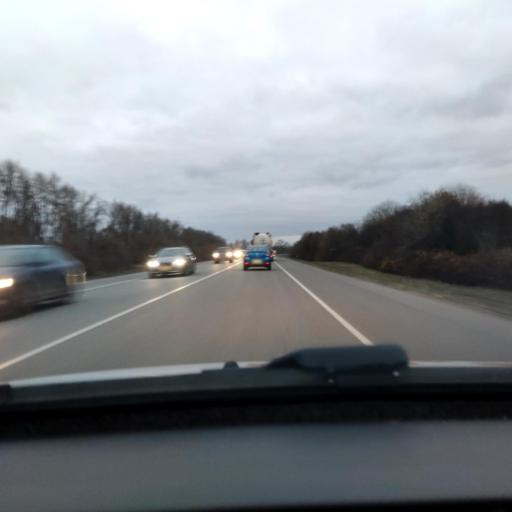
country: RU
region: Lipetsk
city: Borinskoye
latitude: 52.4516
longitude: 39.2969
